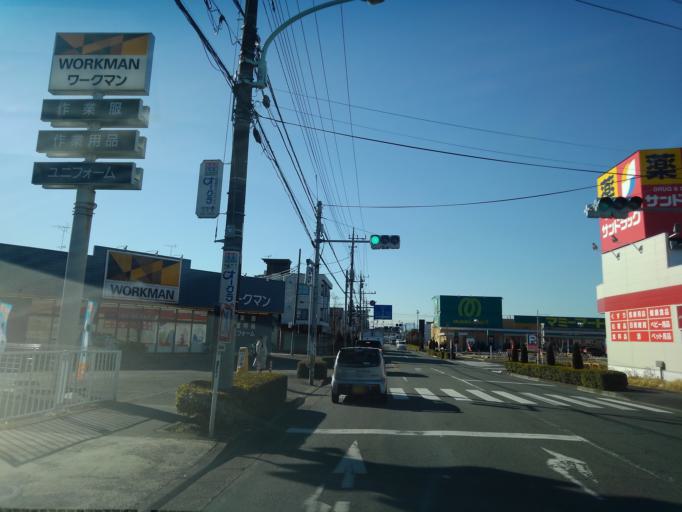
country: JP
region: Tokyo
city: Hino
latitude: 35.6988
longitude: 139.3769
